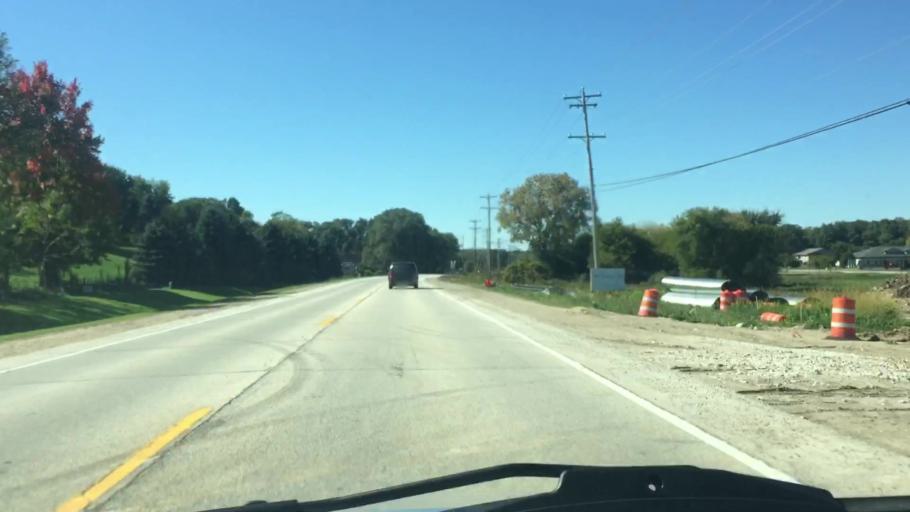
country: US
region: Wisconsin
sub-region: Waukesha County
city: Wales
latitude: 43.0159
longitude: -88.3712
